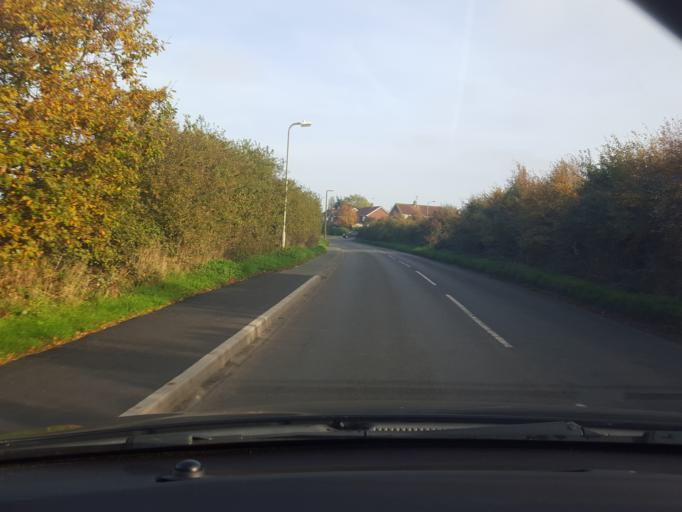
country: GB
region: England
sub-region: Essex
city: Frinton-on-Sea
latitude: 51.8492
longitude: 1.2462
